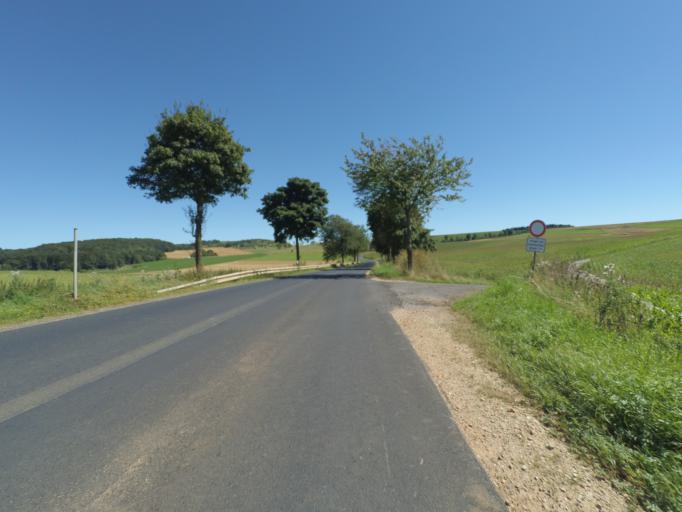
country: DE
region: Rheinland-Pfalz
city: Feusdorf
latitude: 50.3458
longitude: 6.6312
